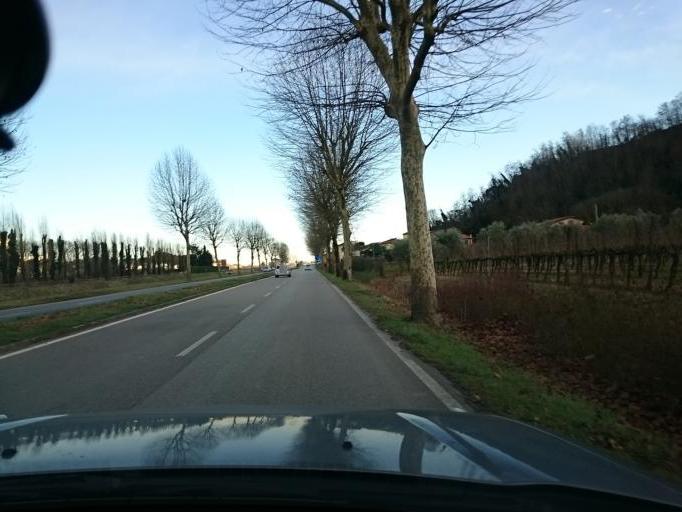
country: IT
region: Veneto
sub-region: Provincia di Padova
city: Montegrotto Terme
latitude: 45.3224
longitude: 11.7811
